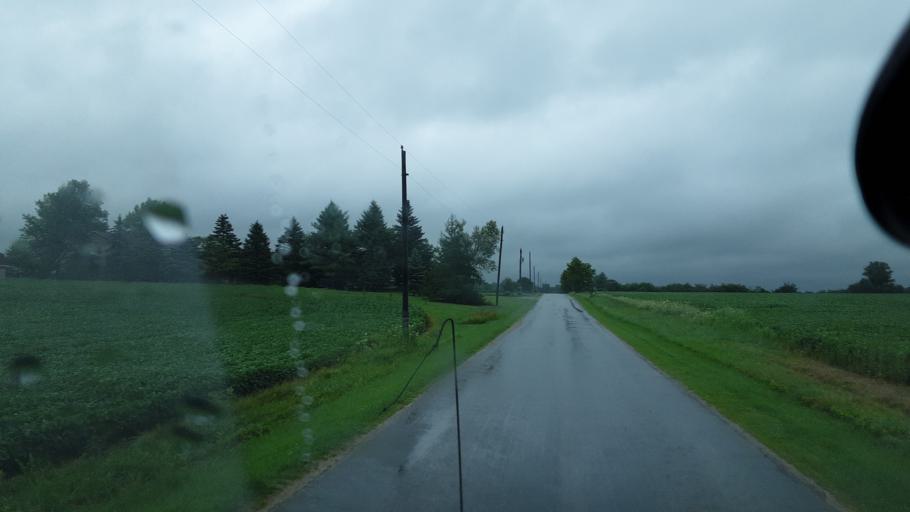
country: US
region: Indiana
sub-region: Adams County
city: Decatur
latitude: 40.7755
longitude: -84.8564
